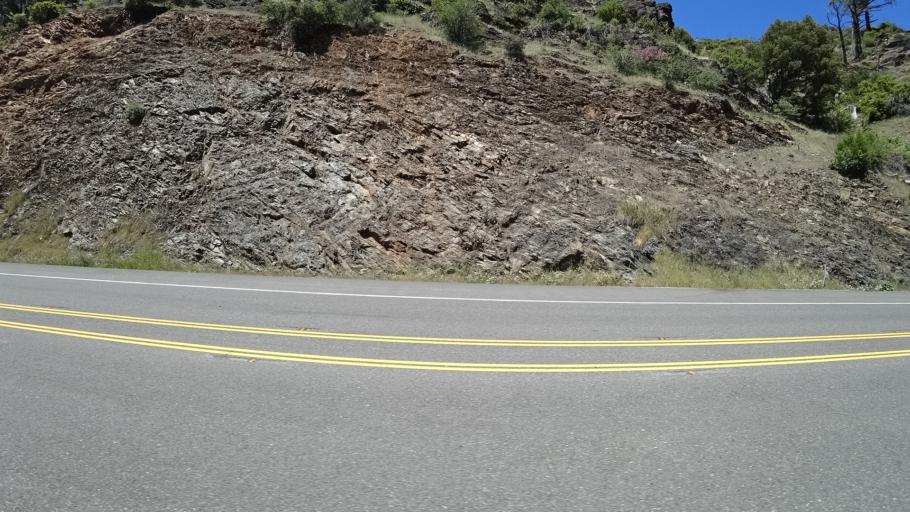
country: US
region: California
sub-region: Trinity County
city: Weaverville
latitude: 40.7423
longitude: -122.9998
